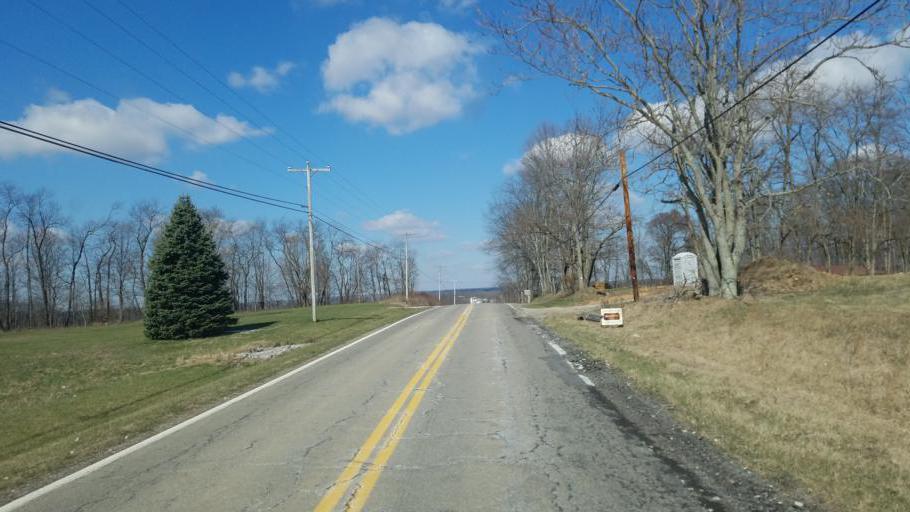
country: US
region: Ohio
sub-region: Licking County
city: Utica
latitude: 40.2437
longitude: -82.4884
